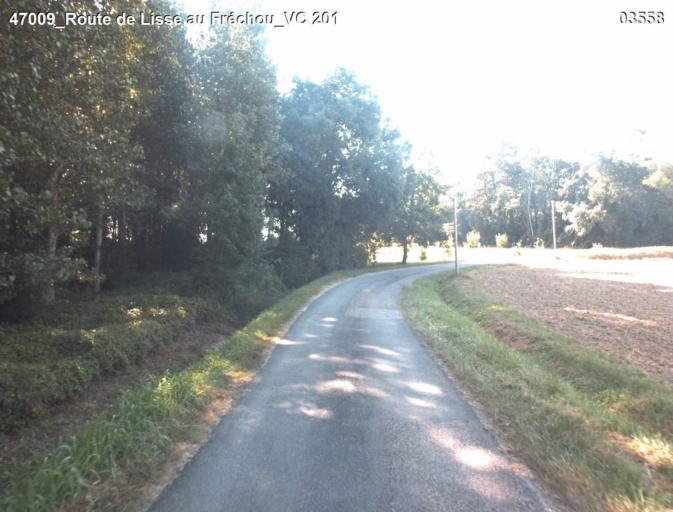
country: FR
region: Aquitaine
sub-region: Departement du Lot-et-Garonne
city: Mezin
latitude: 44.1009
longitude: 0.2758
